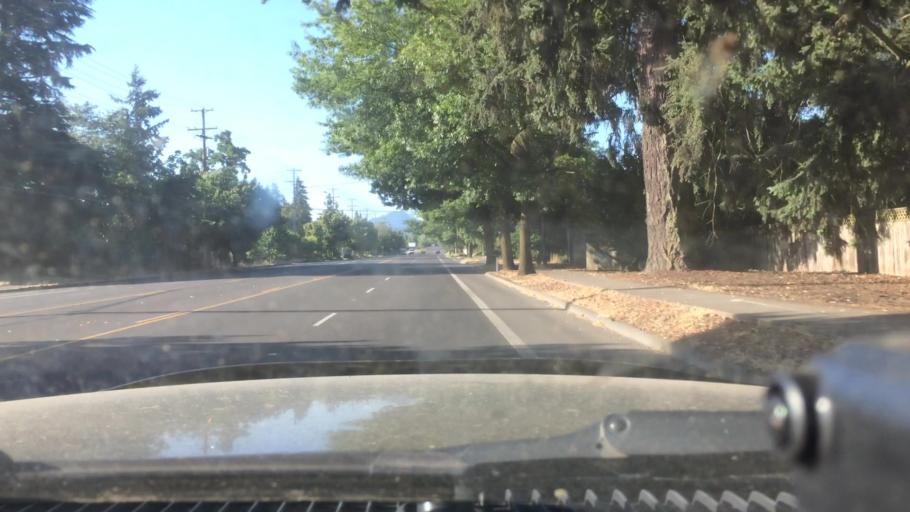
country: US
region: Oregon
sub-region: Lane County
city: Eugene
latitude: 44.0694
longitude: -123.1183
